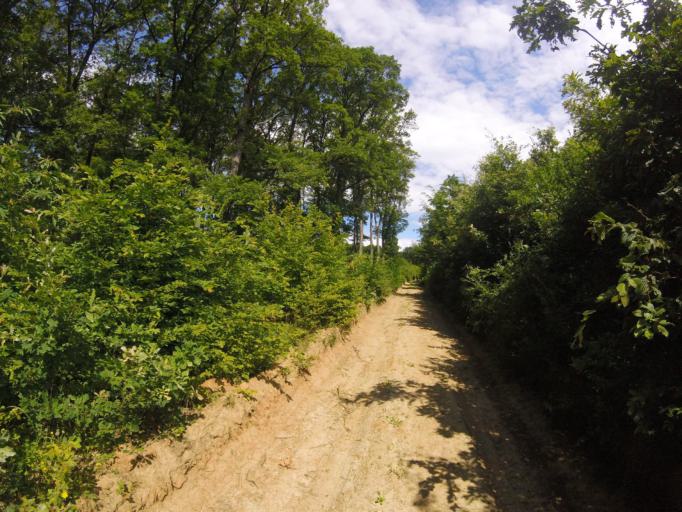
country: HU
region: Nograd
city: Romhany
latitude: 47.8932
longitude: 19.2463
